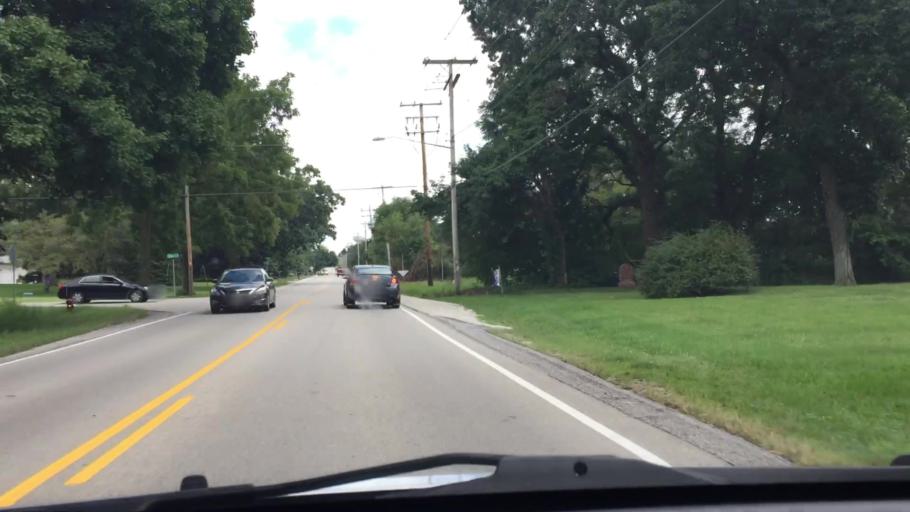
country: US
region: Wisconsin
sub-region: Waukesha County
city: Hartland
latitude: 43.1197
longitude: -88.3283
